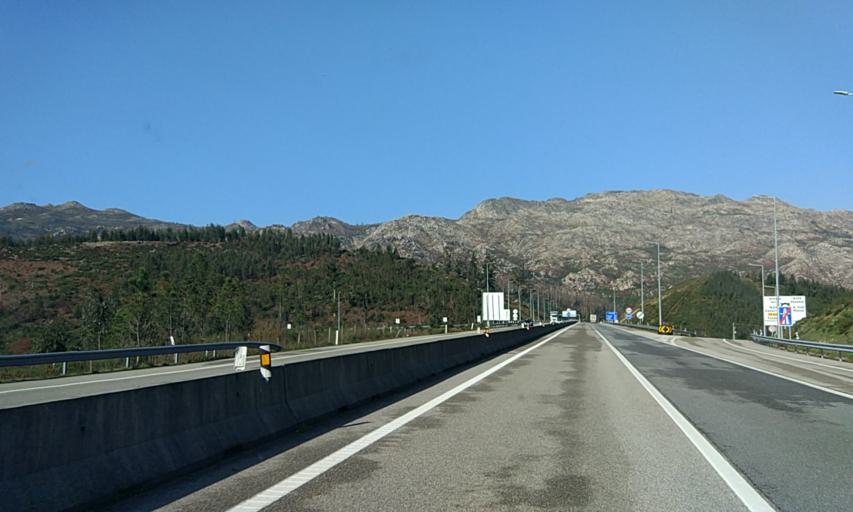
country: PT
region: Viseu
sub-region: Vouzela
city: Vouzela
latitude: 40.6513
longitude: -8.0676
